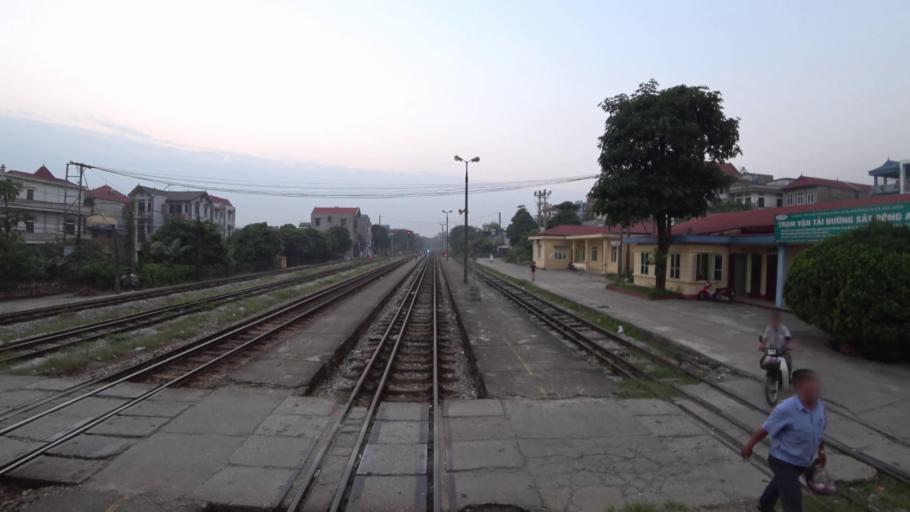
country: VN
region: Ha Noi
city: Soc Son
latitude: 21.2021
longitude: 105.8551
